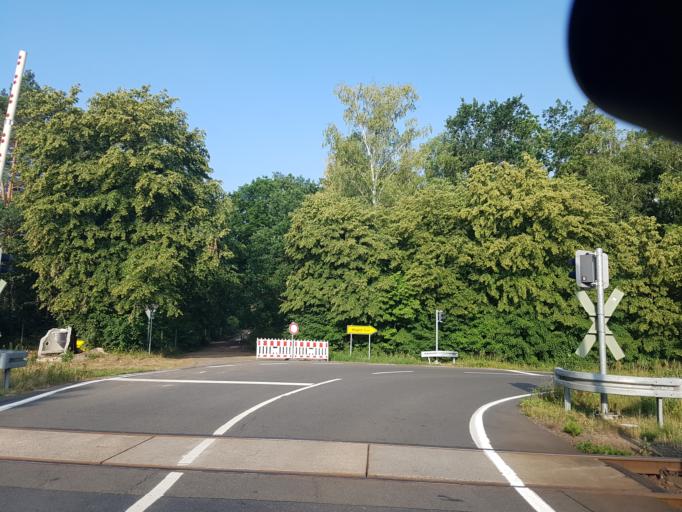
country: DE
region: Saxony-Anhalt
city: Holzdorf
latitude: 51.8517
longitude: 13.0858
